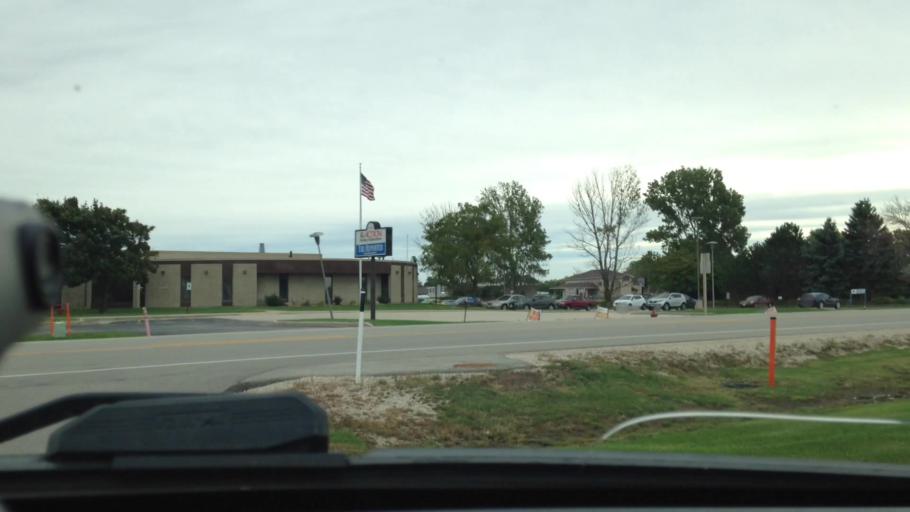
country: US
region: Wisconsin
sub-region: Fond du Lac County
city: North Fond du Lac
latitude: 43.7823
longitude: -88.4850
